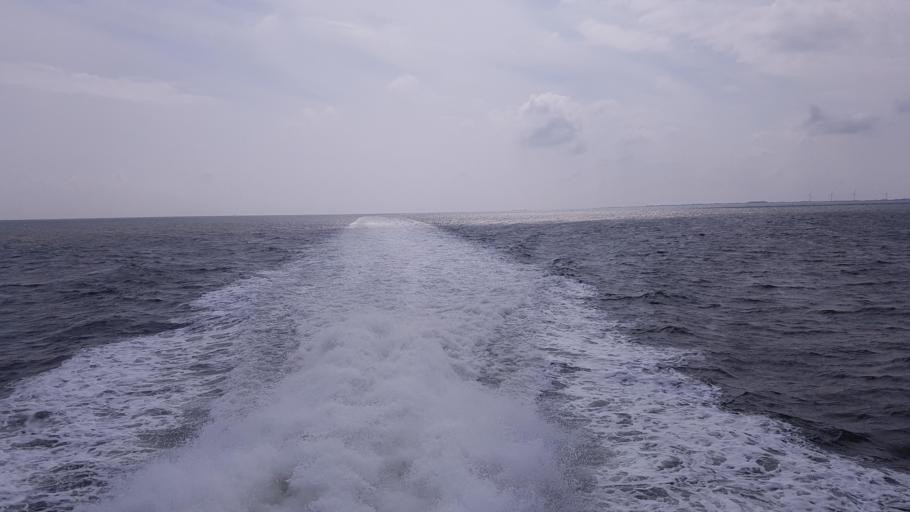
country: DE
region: Schleswig-Holstein
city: Grode
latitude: 54.5759
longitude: 8.7890
